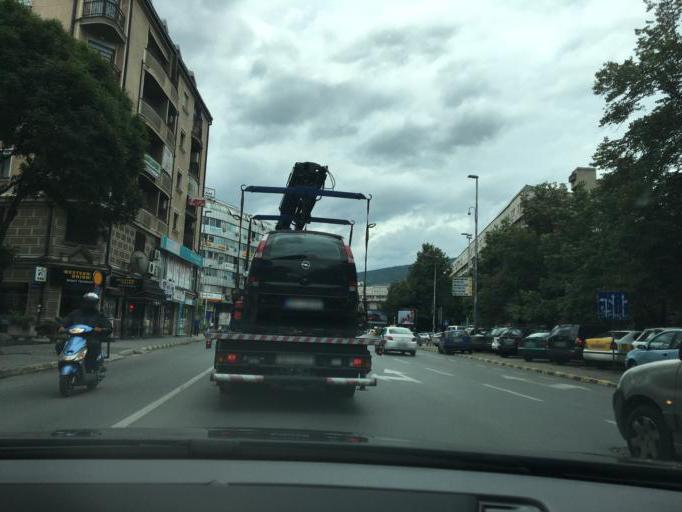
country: MK
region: Karpos
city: Skopje
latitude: 41.9958
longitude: 21.4279
